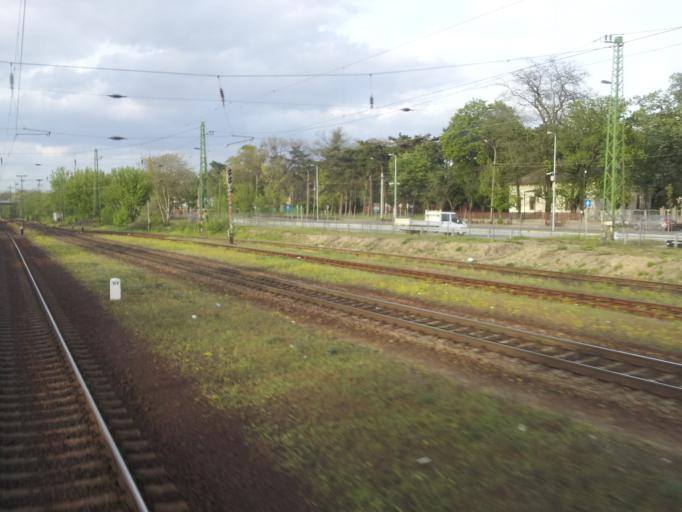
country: HU
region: Pest
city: Dunakeszi
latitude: 47.6266
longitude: 19.1364
